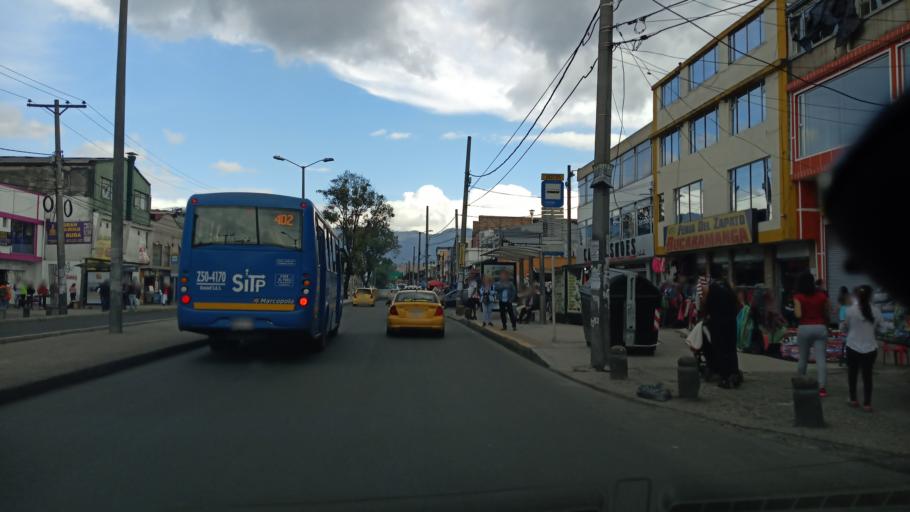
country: CO
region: Bogota D.C.
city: Barrio San Luis
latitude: 4.6822
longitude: -74.0900
